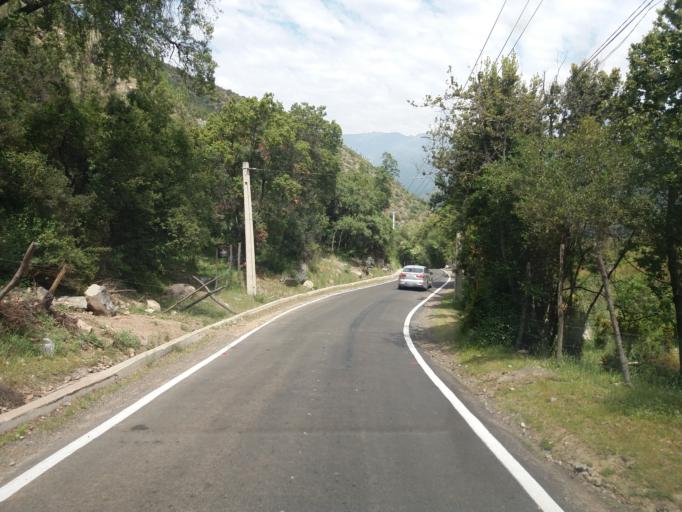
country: CL
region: Valparaiso
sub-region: Provincia de Marga Marga
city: Limache
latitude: -33.0375
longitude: -71.0926
